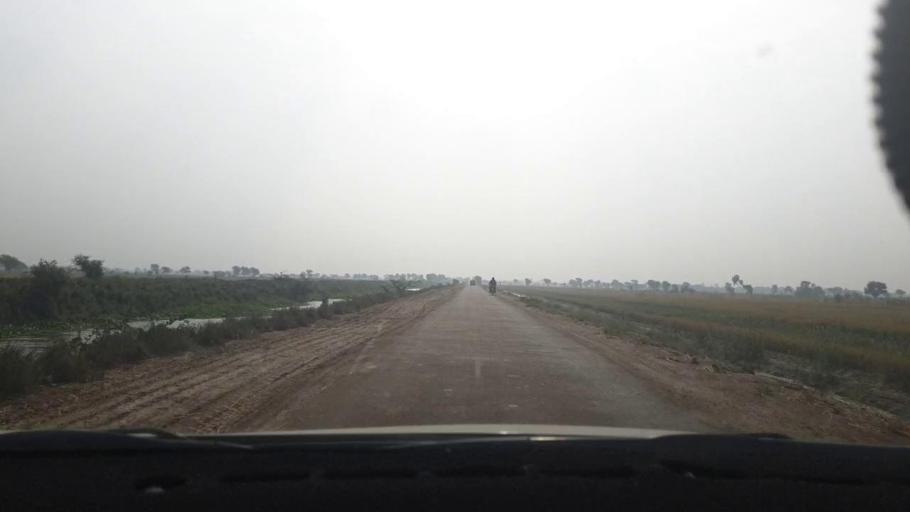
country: PK
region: Sindh
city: Tando Muhammad Khan
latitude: 25.0739
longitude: 68.5354
